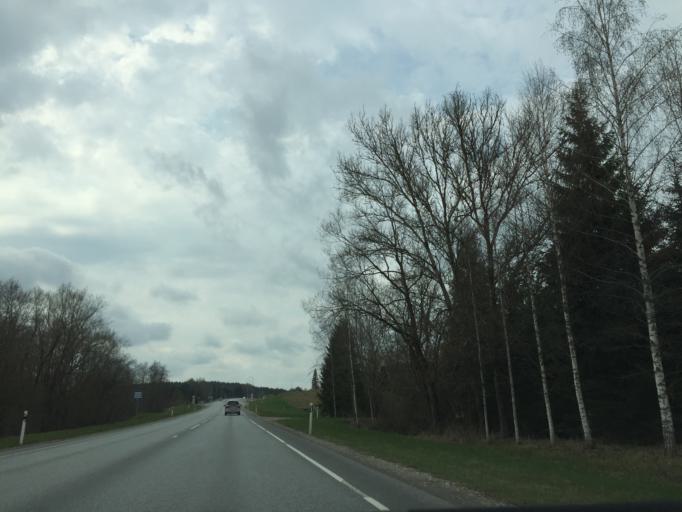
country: EE
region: Tartu
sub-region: Noo vald
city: Noo
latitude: 58.2615
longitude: 26.4793
